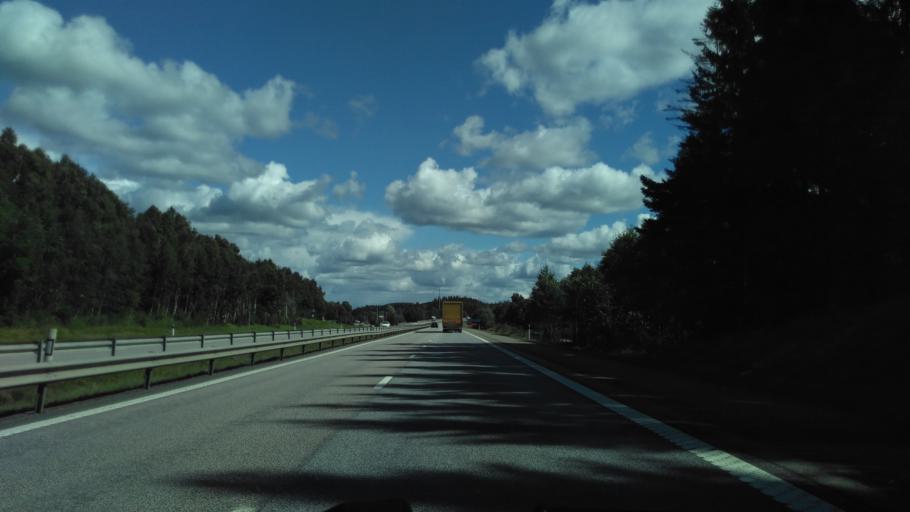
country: SE
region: Vaestra Goetaland
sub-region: Harryda Kommun
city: Landvetter
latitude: 57.6847
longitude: 12.2234
